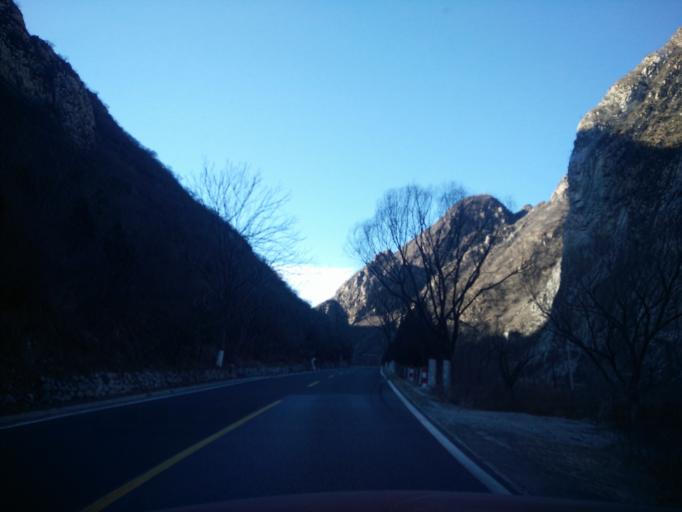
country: CN
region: Beijing
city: Yanchi
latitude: 40.0095
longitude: 115.7909
